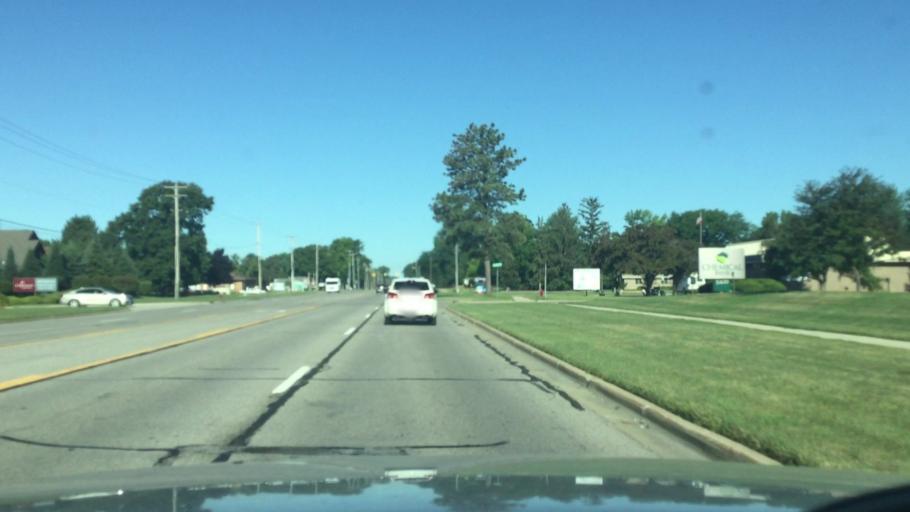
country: US
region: Michigan
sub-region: Saginaw County
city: Shields
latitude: 43.4154
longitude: -84.0228
